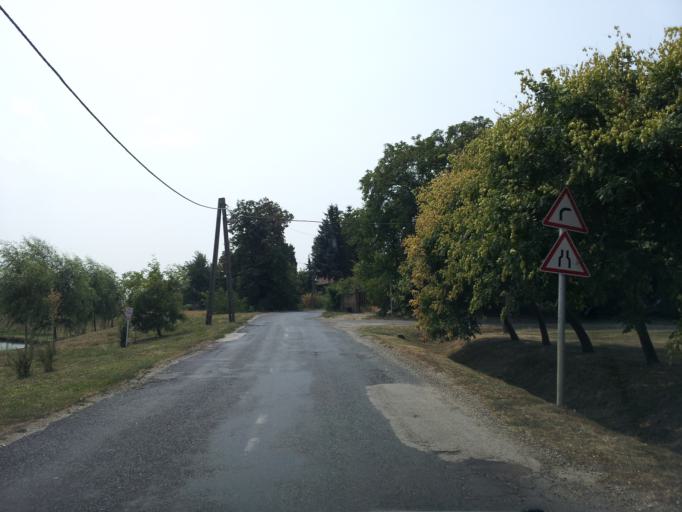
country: HU
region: Gyor-Moson-Sopron
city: Mihalyi
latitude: 47.4979
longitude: 17.1278
